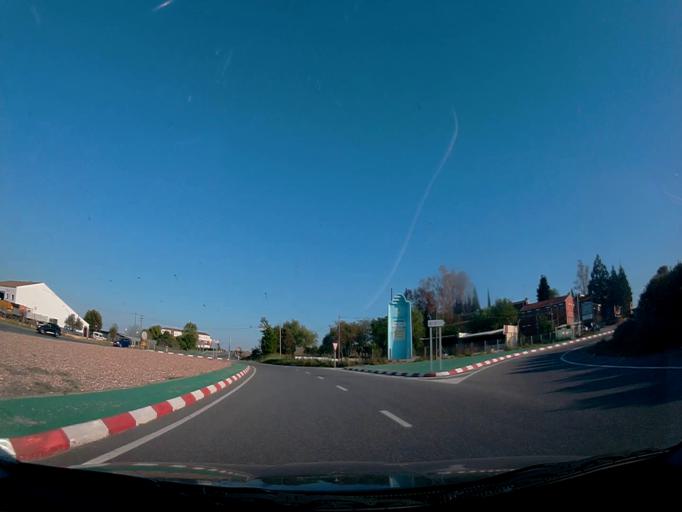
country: ES
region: Castille-La Mancha
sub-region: Province of Toledo
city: Maqueda
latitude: 40.0599
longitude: -4.3697
